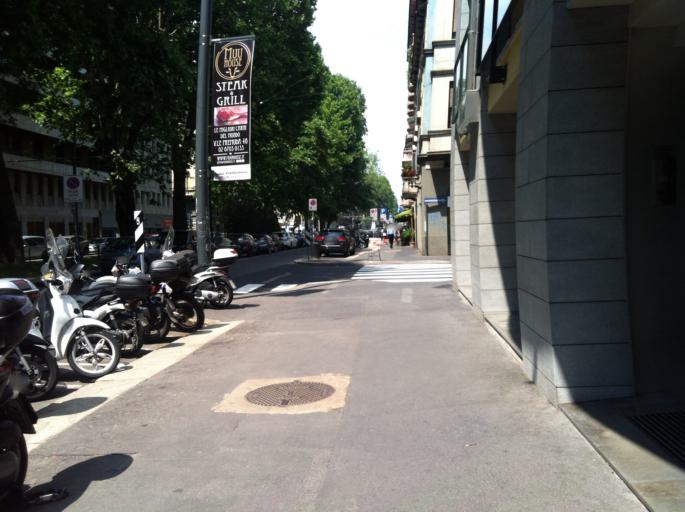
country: IT
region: Lombardy
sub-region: Citta metropolitana di Milano
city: Milano
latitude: 45.4662
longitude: 9.2070
